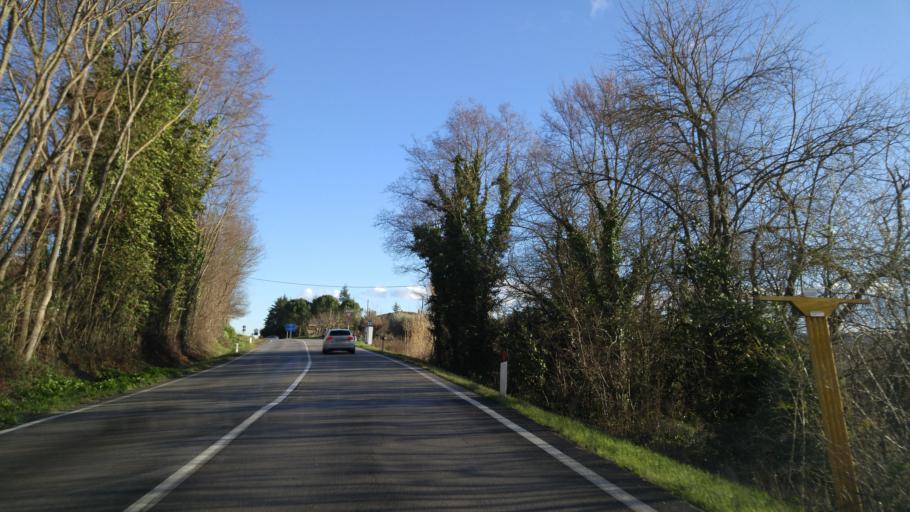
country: IT
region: The Marches
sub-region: Provincia di Ancona
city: Camerano
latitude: 43.5084
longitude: 13.5444
